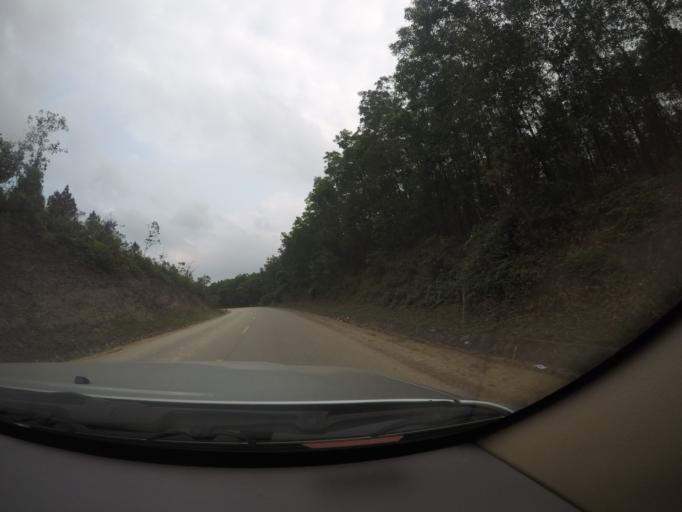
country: VN
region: Quang Binh
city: Kien Giang
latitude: 17.1325
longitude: 106.7763
